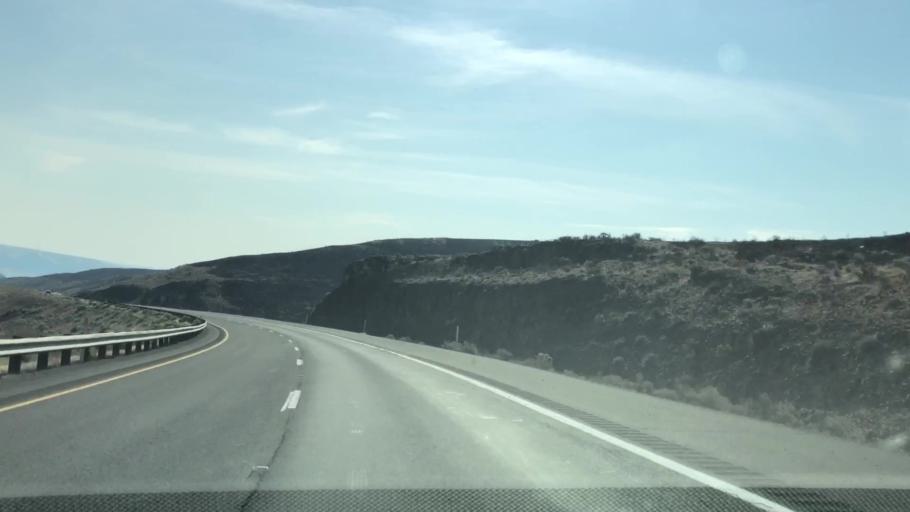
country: US
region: Washington
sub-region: Grant County
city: Mattawa
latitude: 46.9385
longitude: -120.0425
